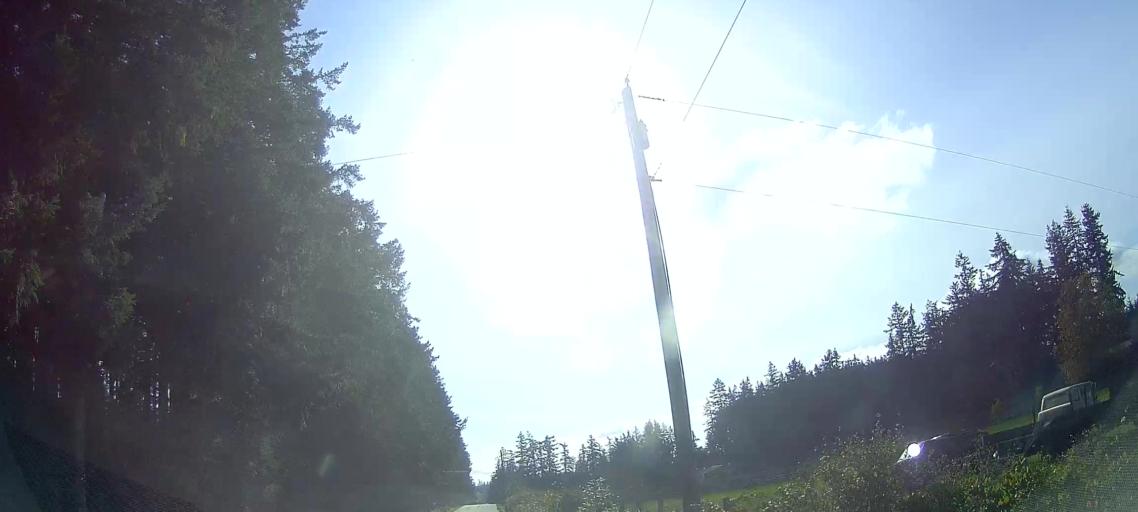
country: US
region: Washington
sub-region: Island County
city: Camano
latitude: 48.2099
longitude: -122.4562
